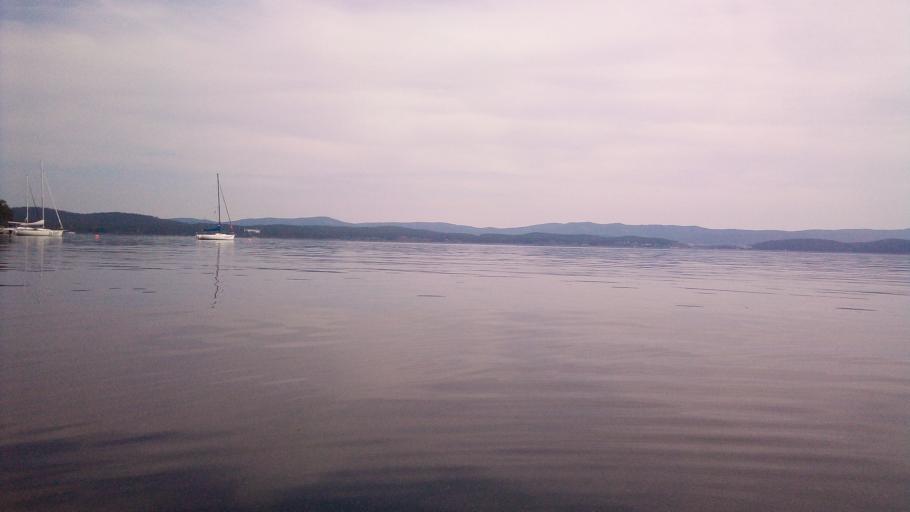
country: RU
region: Chelyabinsk
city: Turgoyak
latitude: 55.1769
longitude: 60.0350
